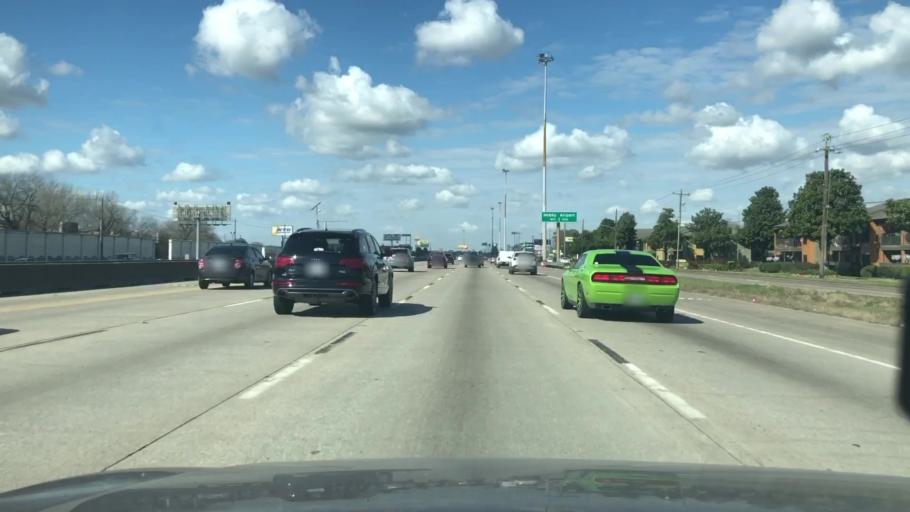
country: US
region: Texas
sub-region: Harris County
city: South Houston
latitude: 29.6353
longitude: -95.2361
